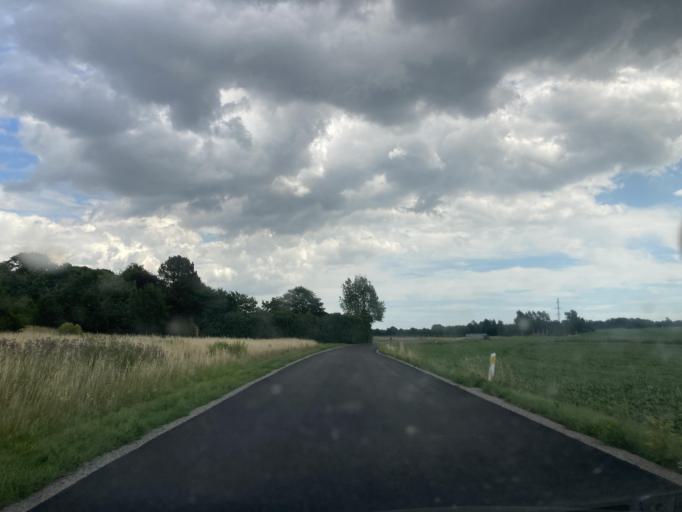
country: DK
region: Zealand
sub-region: Faxe Kommune
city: Haslev
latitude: 55.3331
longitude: 11.9994
